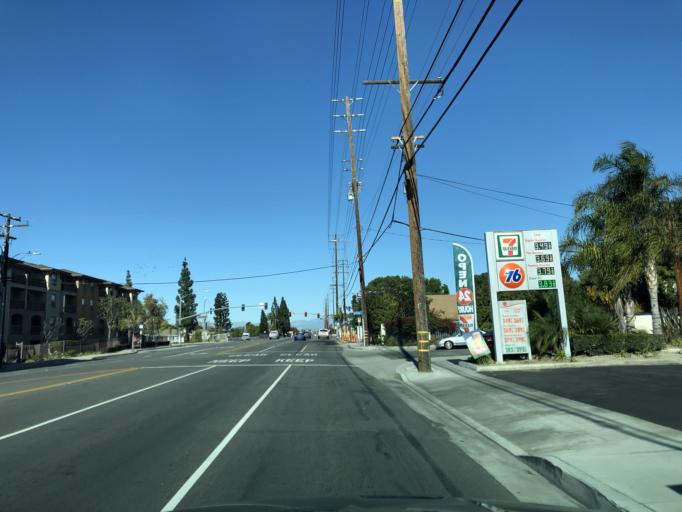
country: US
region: California
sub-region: Orange County
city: Orange
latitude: 33.7783
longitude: -117.8356
